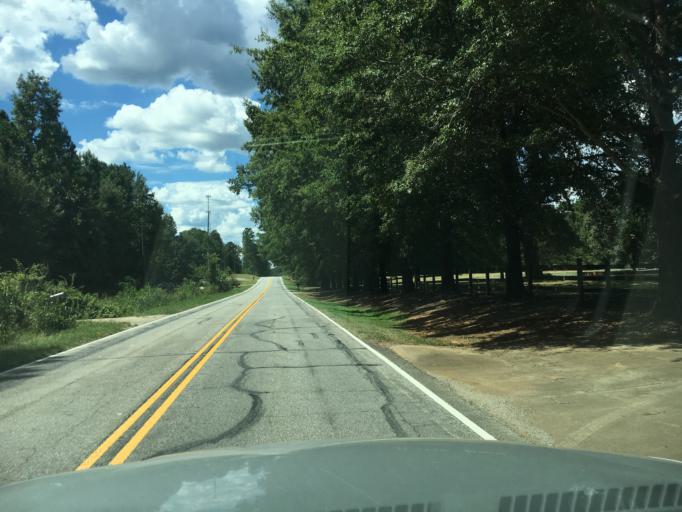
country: US
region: South Carolina
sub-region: Laurens County
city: Laurens
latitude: 34.5196
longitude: -82.1109
